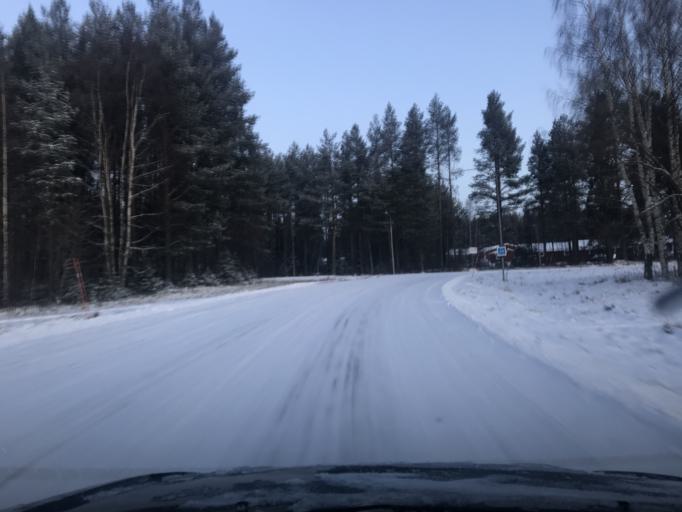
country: SE
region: Norrbotten
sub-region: Lulea Kommun
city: Bergnaset
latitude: 65.6176
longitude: 22.1219
